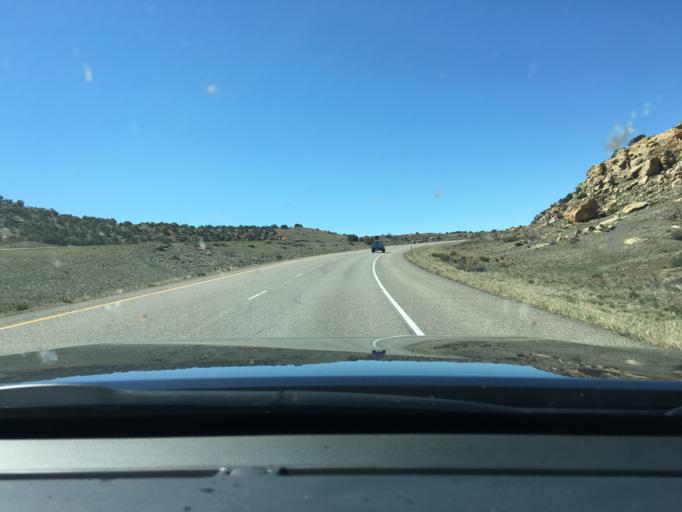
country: US
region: Colorado
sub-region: Mesa County
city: Loma
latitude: 39.1884
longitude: -109.0328
